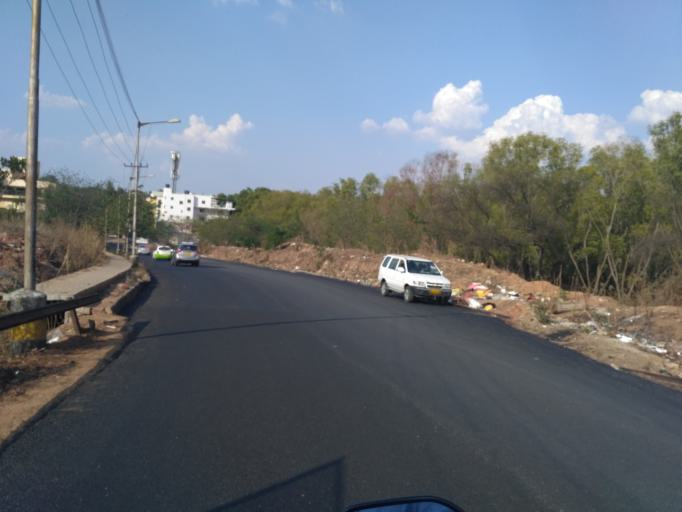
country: IN
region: Karnataka
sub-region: Bangalore Urban
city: Yelahanka
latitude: 13.0441
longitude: 77.5398
